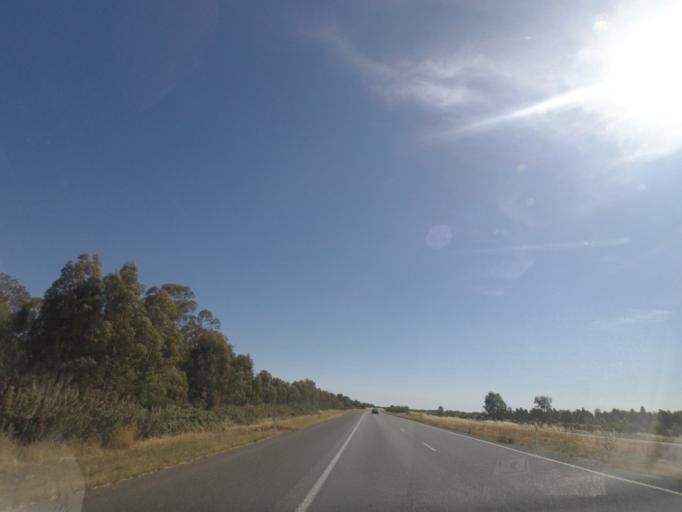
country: AU
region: Victoria
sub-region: Greater Shepparton
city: Shepparton
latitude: -36.6640
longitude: 145.2761
